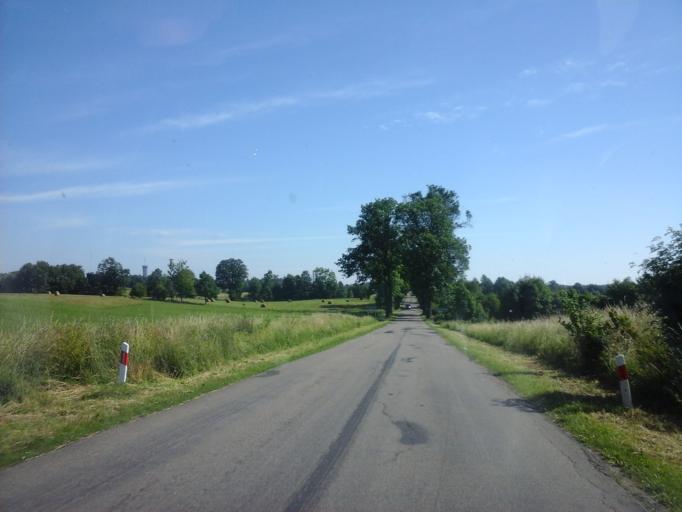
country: PL
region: West Pomeranian Voivodeship
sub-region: Powiat swidwinski
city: Polczyn-Zdroj
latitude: 53.7023
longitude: 16.0609
